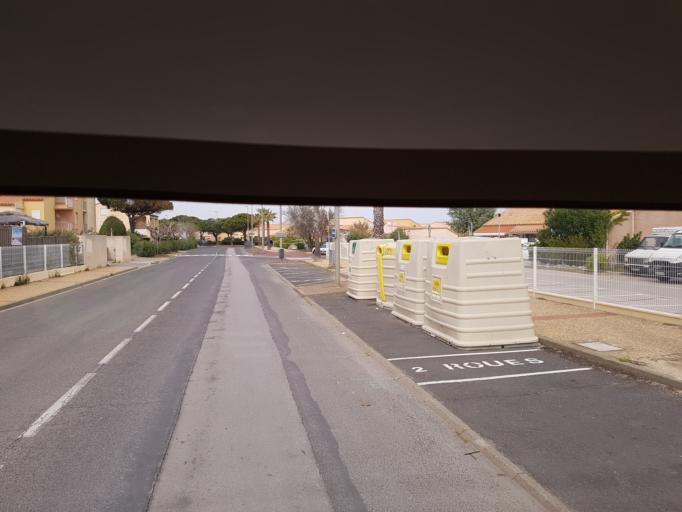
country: FR
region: Languedoc-Roussillon
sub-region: Departement de l'Aude
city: Fleury
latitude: 43.1834
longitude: 3.1952
